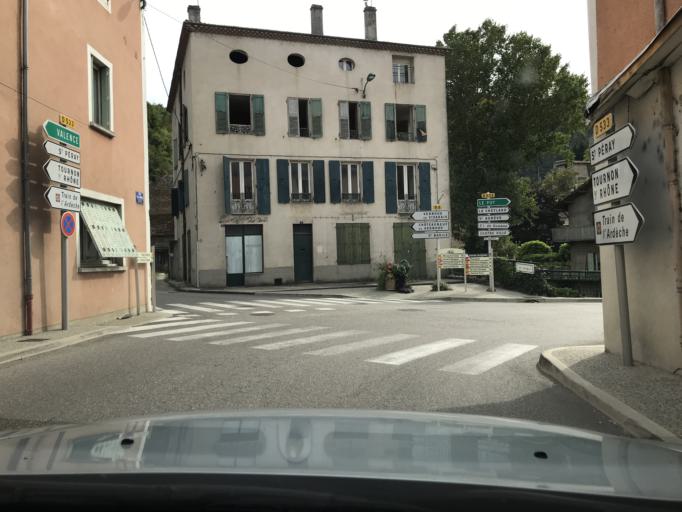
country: FR
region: Rhone-Alpes
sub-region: Departement de l'Ardeche
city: Lamastre
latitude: 44.9856
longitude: 4.5821
